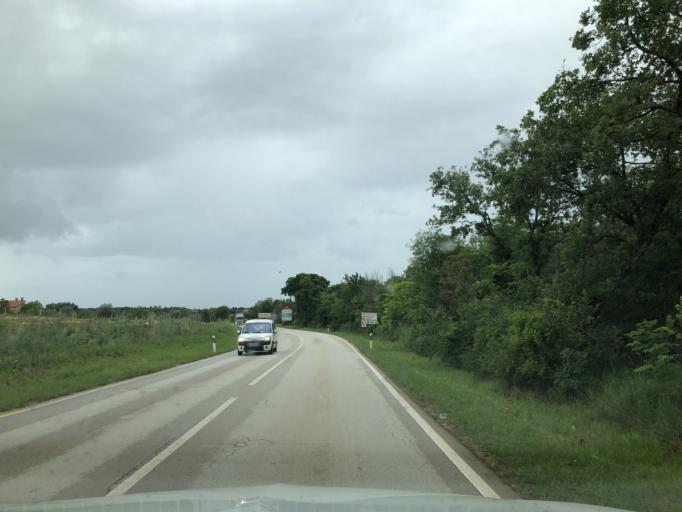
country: HR
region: Istarska
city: Umag
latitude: 45.4498
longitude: 13.5698
